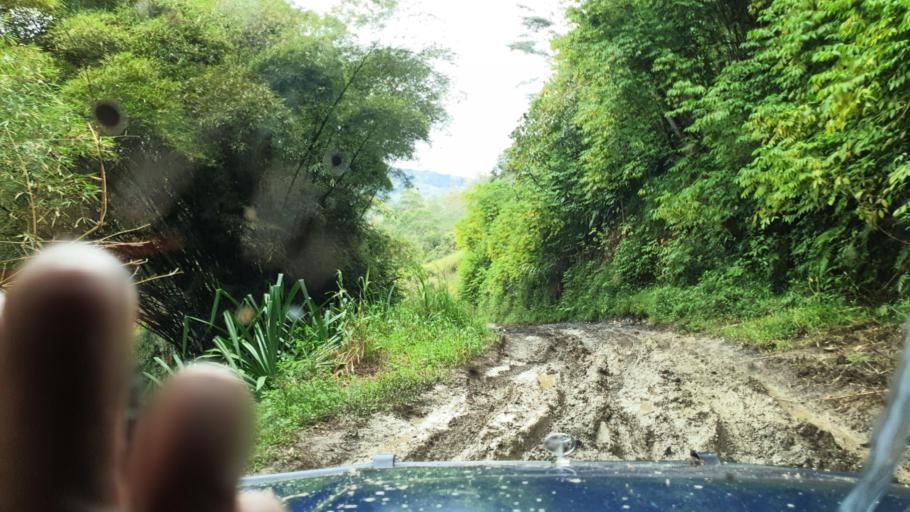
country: PG
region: Jiwaka
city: Minj
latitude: -5.9262
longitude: 144.7431
